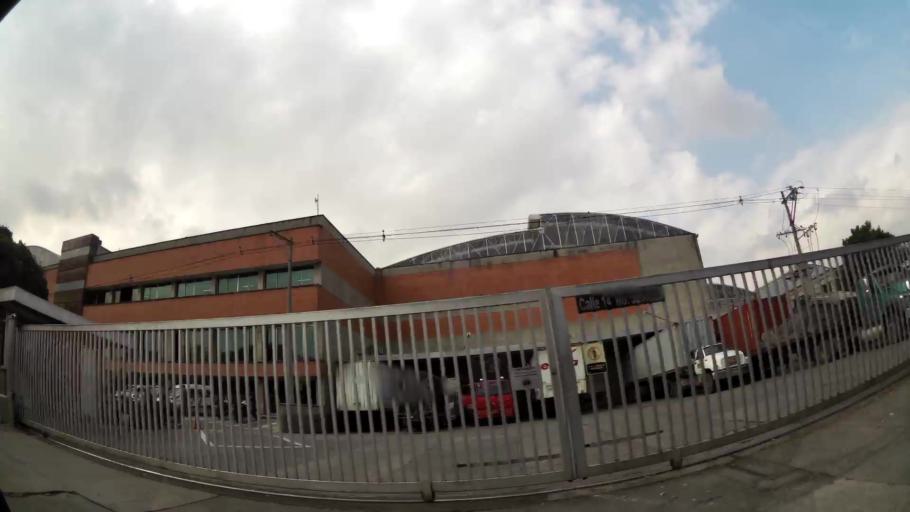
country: CO
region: Antioquia
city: Itagui
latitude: 6.2183
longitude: -75.5835
